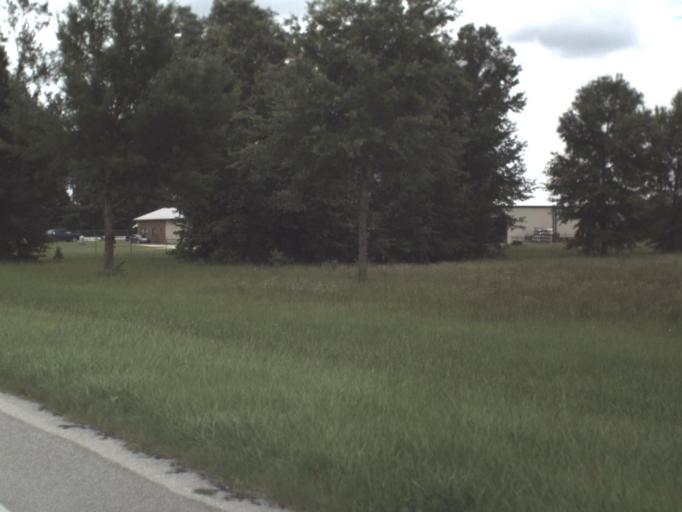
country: US
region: Florida
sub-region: Alachua County
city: Newberry
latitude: 29.7062
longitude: -82.6071
